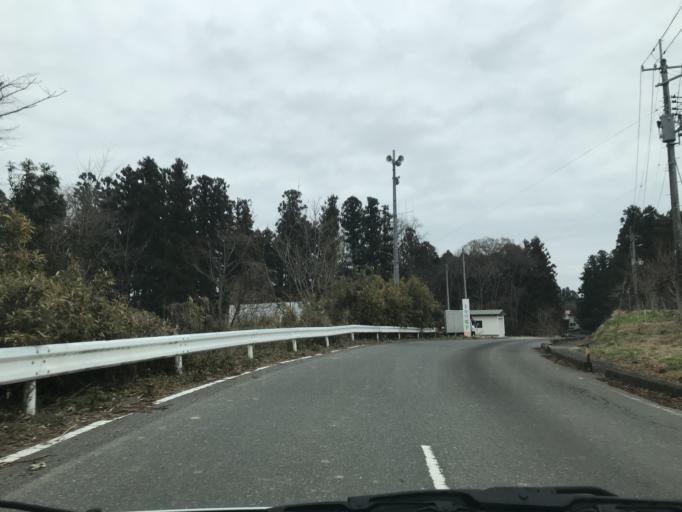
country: JP
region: Iwate
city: Ichinoseki
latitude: 38.7388
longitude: 141.2500
